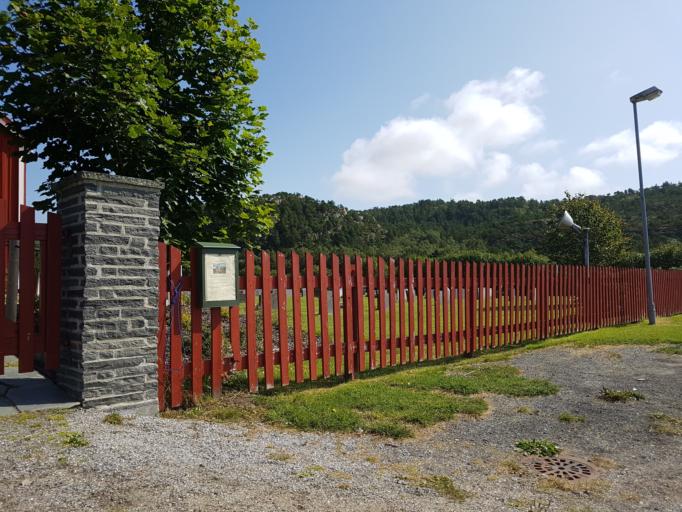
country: NO
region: Sor-Trondelag
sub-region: Agdenes
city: Lensvik
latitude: 63.6315
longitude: 9.8397
